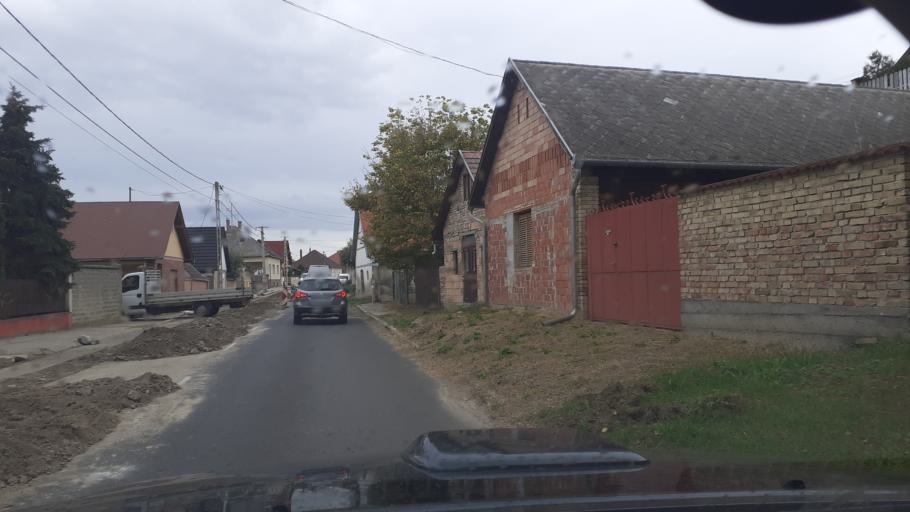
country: HU
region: Tolna
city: Dunafoldvar
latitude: 46.8002
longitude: 18.9311
